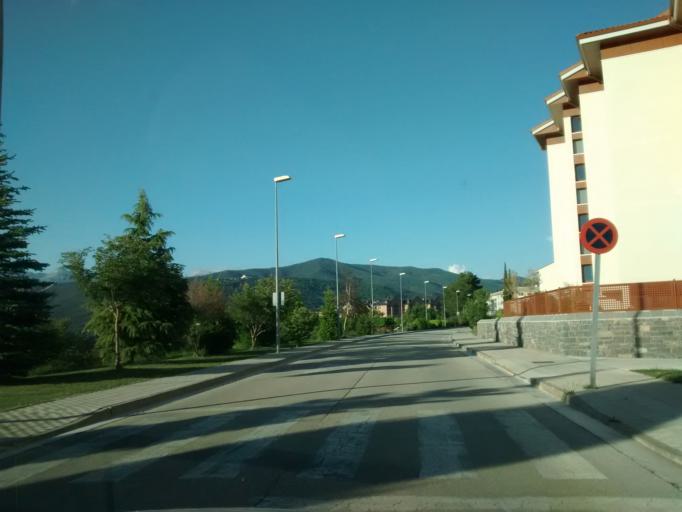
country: ES
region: Aragon
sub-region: Provincia de Huesca
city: Jaca
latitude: 42.5663
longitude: -0.5634
